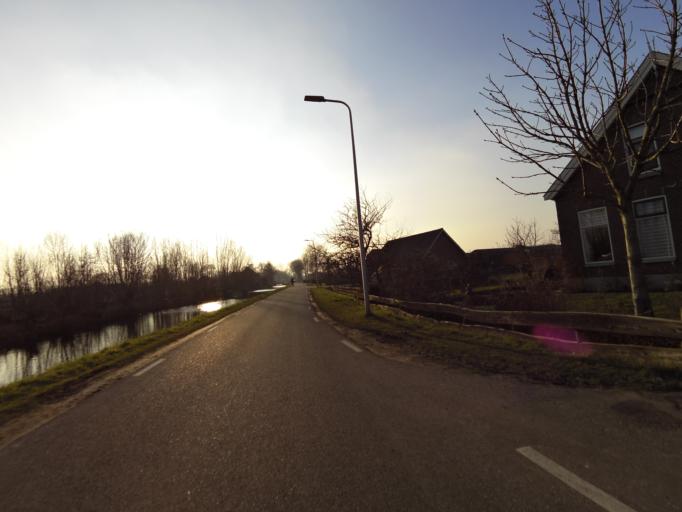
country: NL
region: South Holland
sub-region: Gemeente Alphen aan den Rijn
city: Alphen aan den Rijn
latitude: 52.1414
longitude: 4.6138
